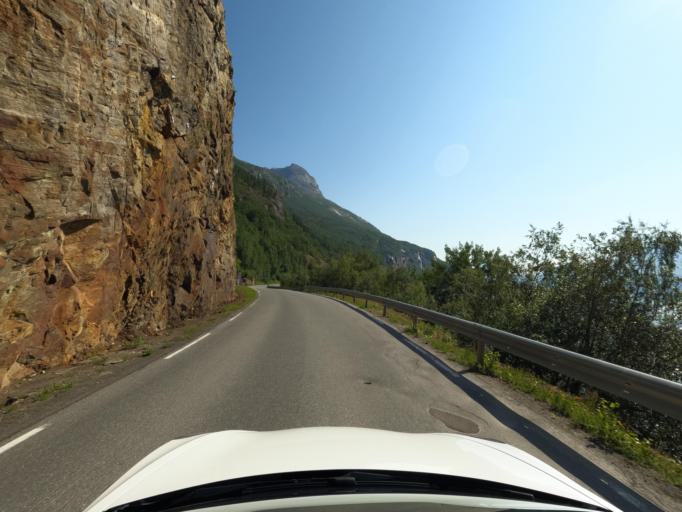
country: NO
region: Nordland
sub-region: Narvik
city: Narvik
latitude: 68.3595
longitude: 17.2656
